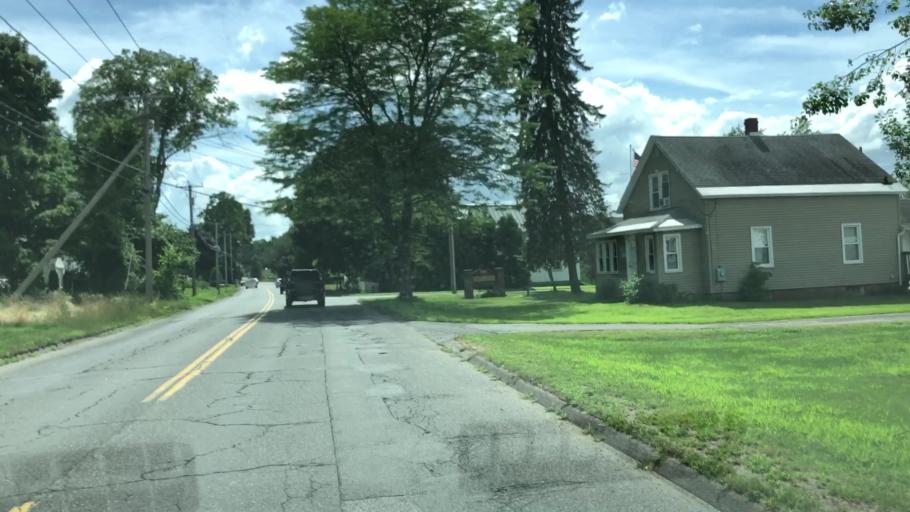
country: US
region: Massachusetts
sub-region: Hampshire County
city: Easthampton
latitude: 42.2782
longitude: -72.6368
